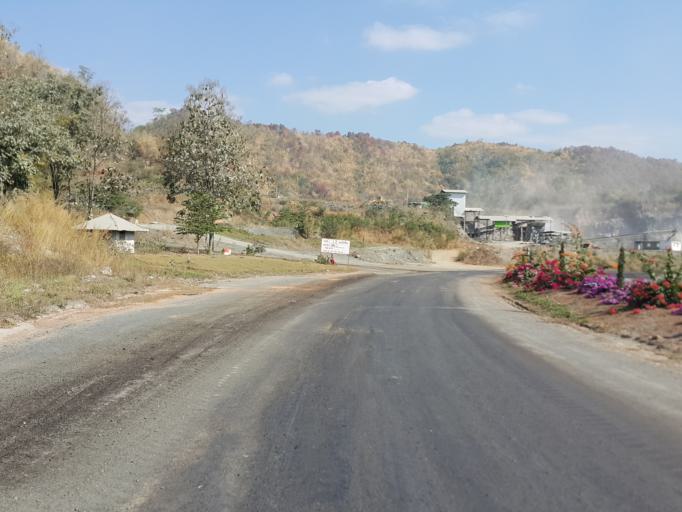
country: TH
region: Chiang Mai
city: Mae On
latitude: 18.8406
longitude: 99.2291
